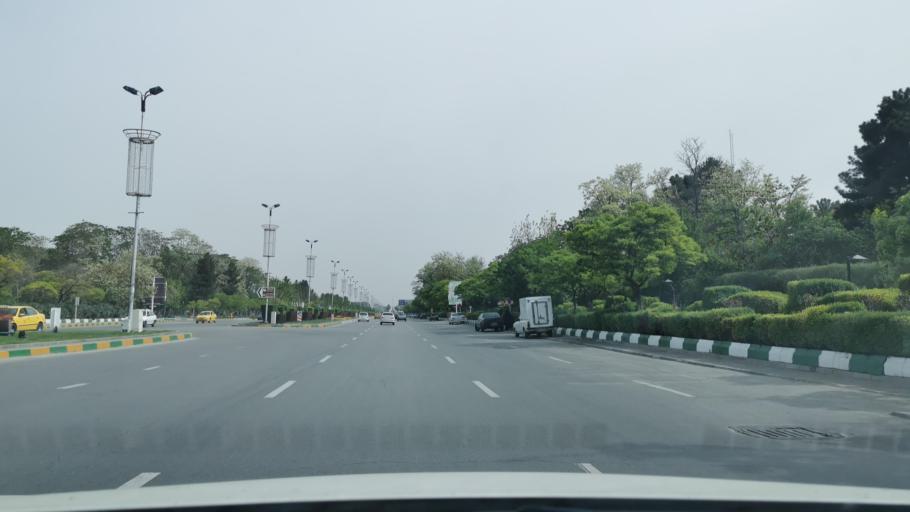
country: IR
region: Razavi Khorasan
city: Mashhad
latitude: 36.2509
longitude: 59.6157
